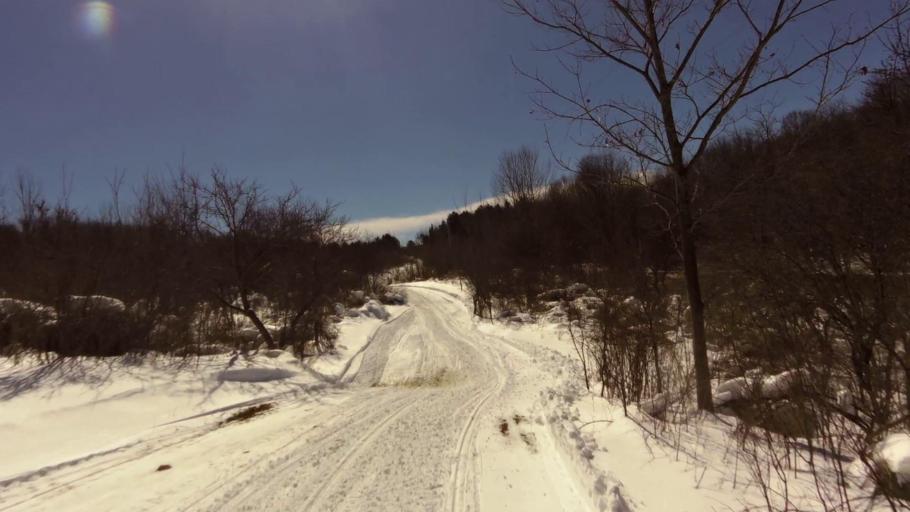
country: US
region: New York
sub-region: Allegany County
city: Cuba
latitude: 42.3310
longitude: -78.2498
